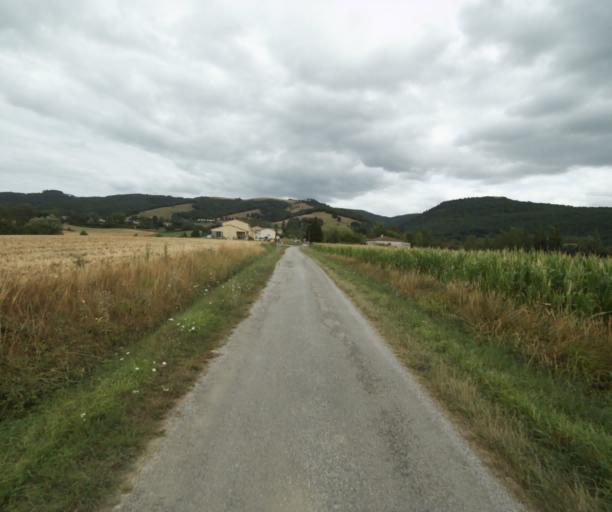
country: FR
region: Midi-Pyrenees
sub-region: Departement du Tarn
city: Soreze
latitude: 43.4594
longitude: 2.0688
